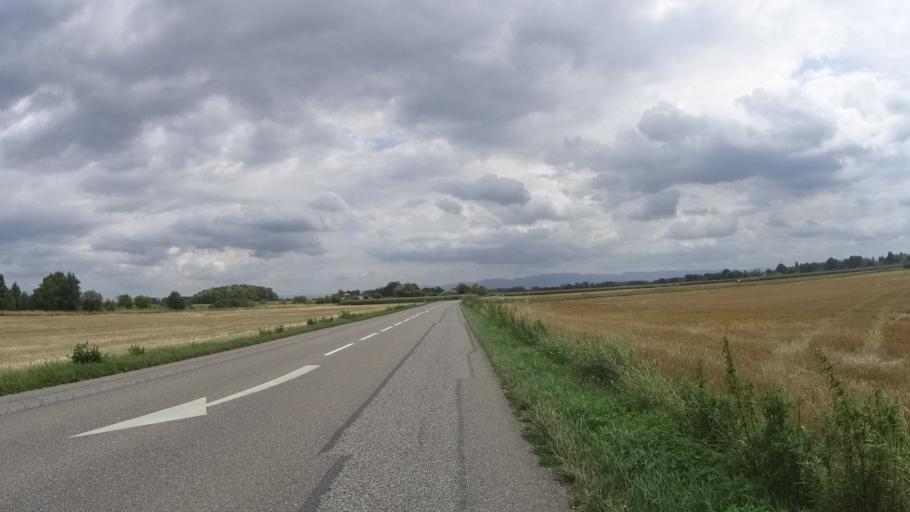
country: FR
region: Alsace
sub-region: Departement du Bas-Rhin
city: Weyersheim
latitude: 48.7092
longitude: 7.8181
